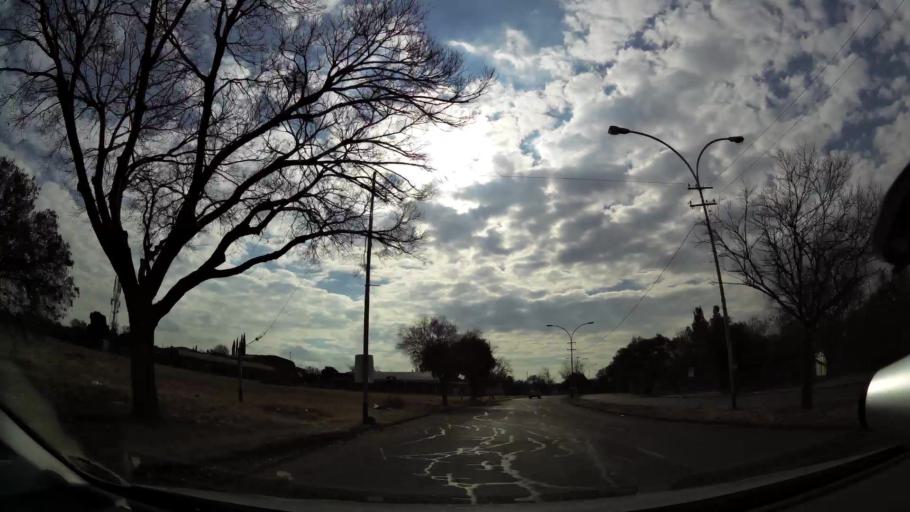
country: ZA
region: Orange Free State
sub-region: Mangaung Metropolitan Municipality
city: Bloemfontein
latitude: -29.0856
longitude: 26.2447
